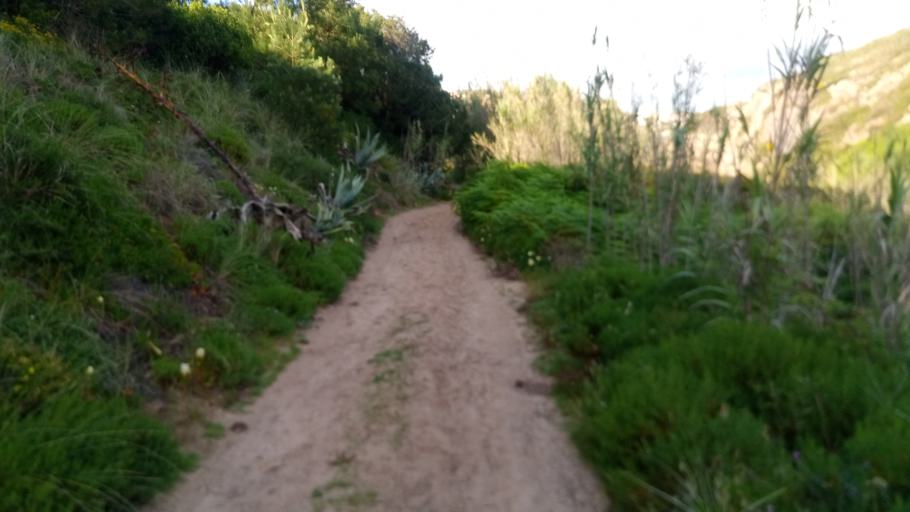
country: PT
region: Leiria
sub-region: Caldas da Rainha
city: Caldas da Rainha
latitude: 39.5076
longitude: -9.1490
